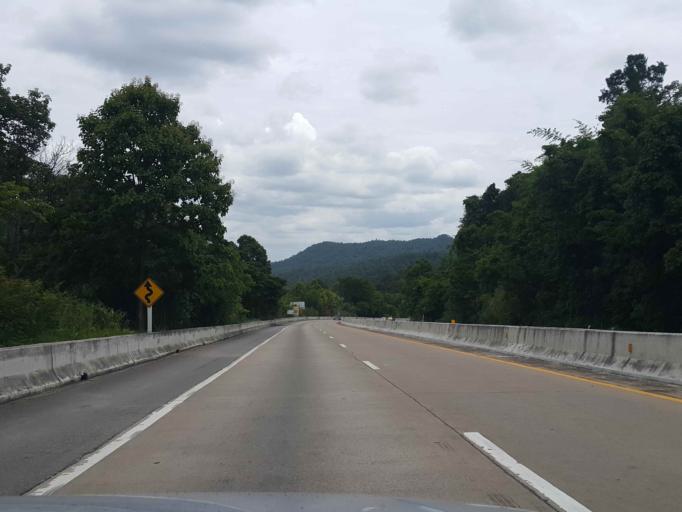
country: TH
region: Lamphun
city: Mae Tha
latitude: 18.4212
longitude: 99.2094
